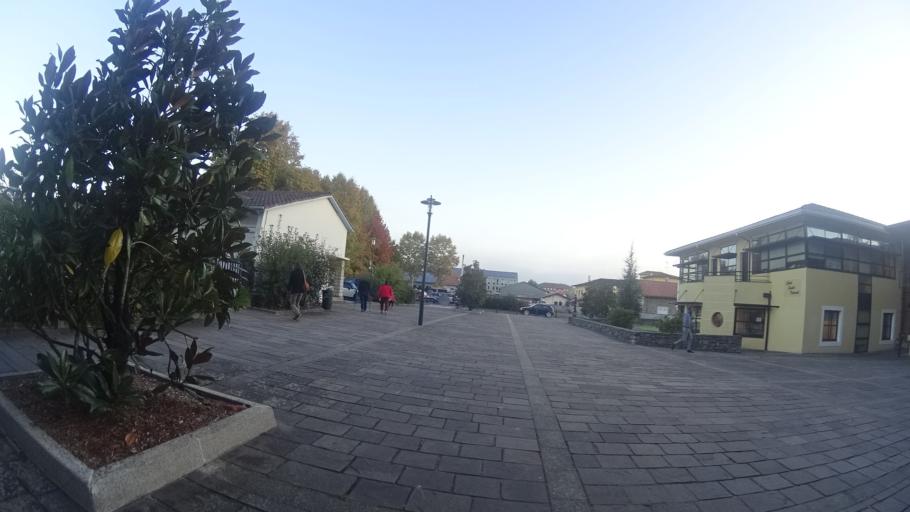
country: FR
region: Aquitaine
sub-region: Departement des Landes
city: Saint-Paul-les-Dax
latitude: 43.7250
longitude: -1.0516
